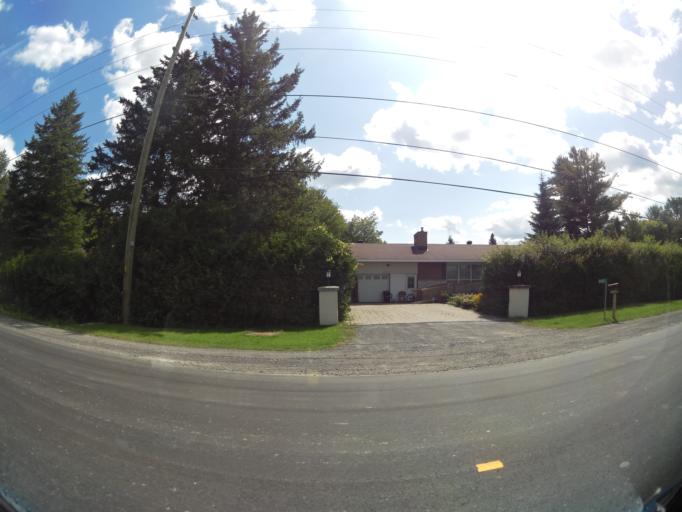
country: CA
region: Ontario
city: Ottawa
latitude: 45.4358
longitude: -75.5027
